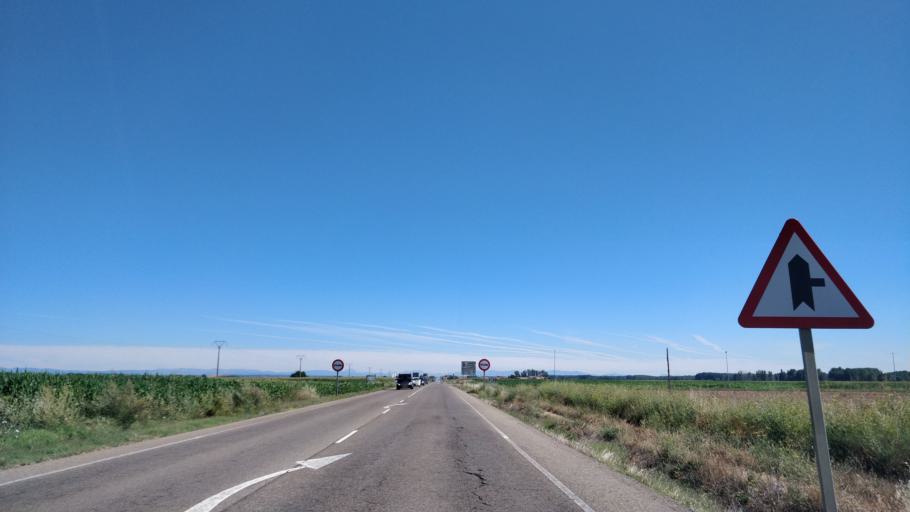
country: ES
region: Castille and Leon
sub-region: Provincia de Leon
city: Soto de la Vega
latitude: 42.3621
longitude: -5.8899
